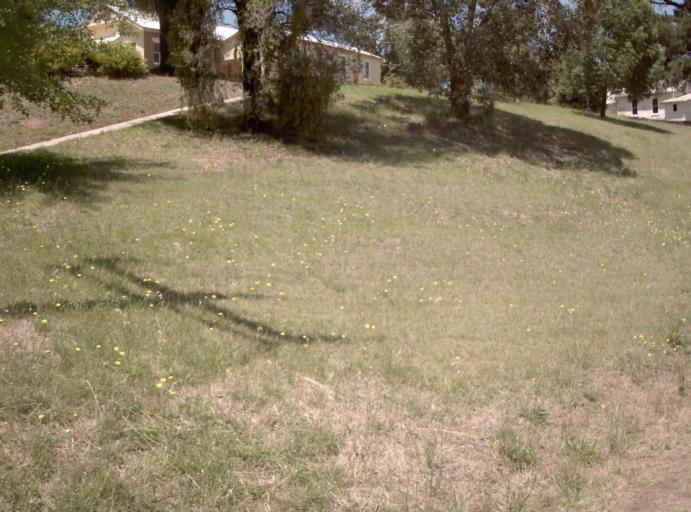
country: AU
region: Victoria
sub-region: East Gippsland
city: Bairnsdale
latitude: -37.3749
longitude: 147.8366
